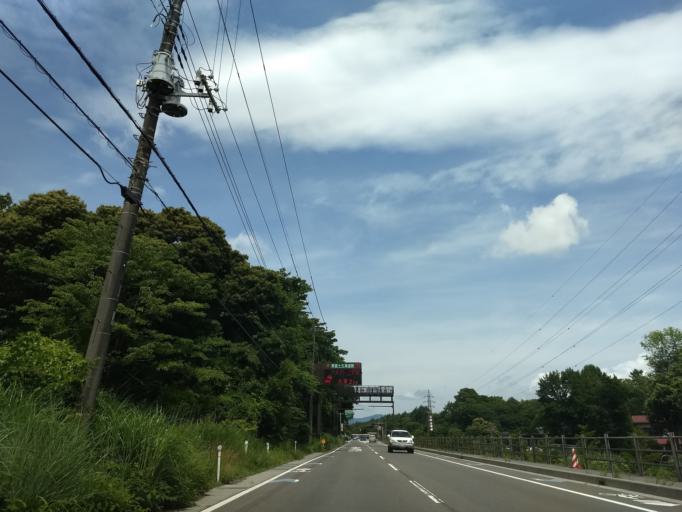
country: JP
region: Yamanashi
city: Fujikawaguchiko
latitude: 35.4342
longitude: 138.8413
